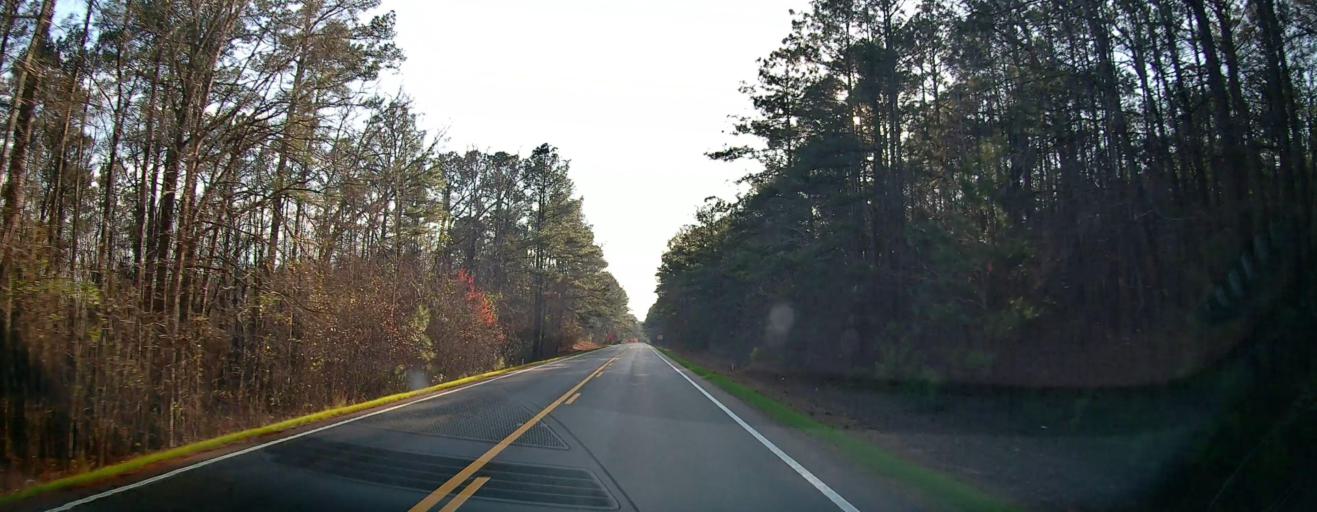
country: US
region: Georgia
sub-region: Harris County
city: Hamilton
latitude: 32.7476
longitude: -84.9391
